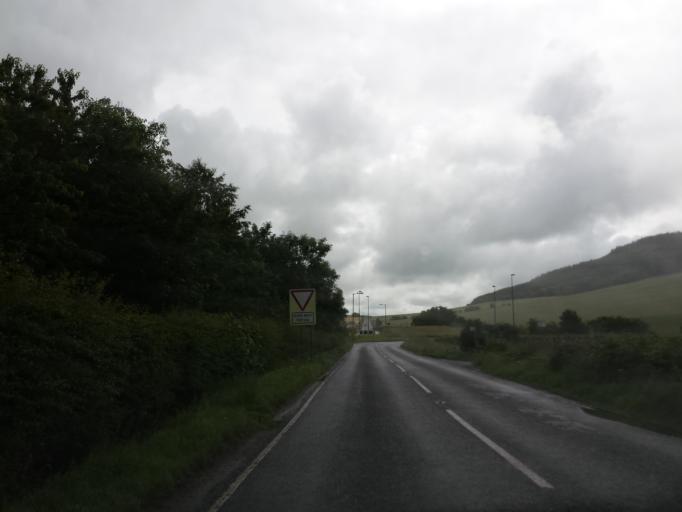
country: GB
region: Scotland
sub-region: Fife
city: Ladybank
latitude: 56.3447
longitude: -3.0979
